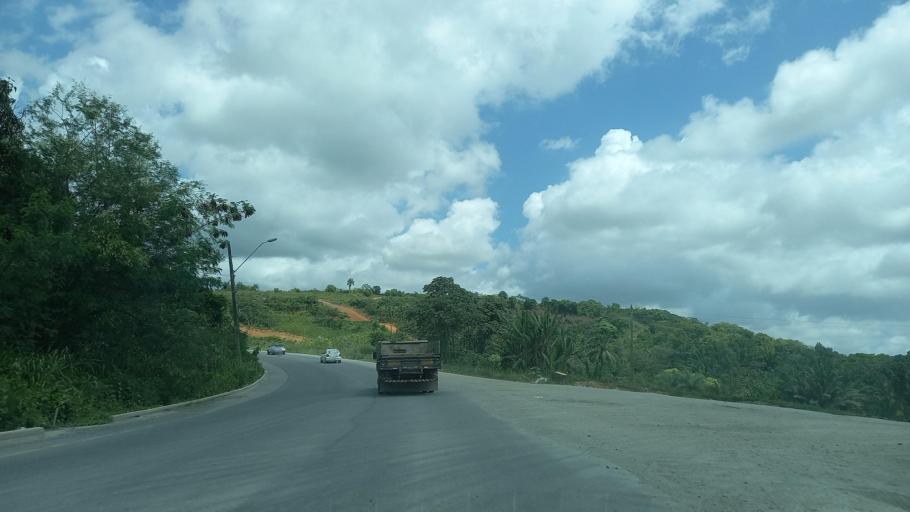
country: BR
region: Pernambuco
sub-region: Jaboatao Dos Guararapes
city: Jaboatao dos Guararapes
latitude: -8.1329
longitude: -35.0043
